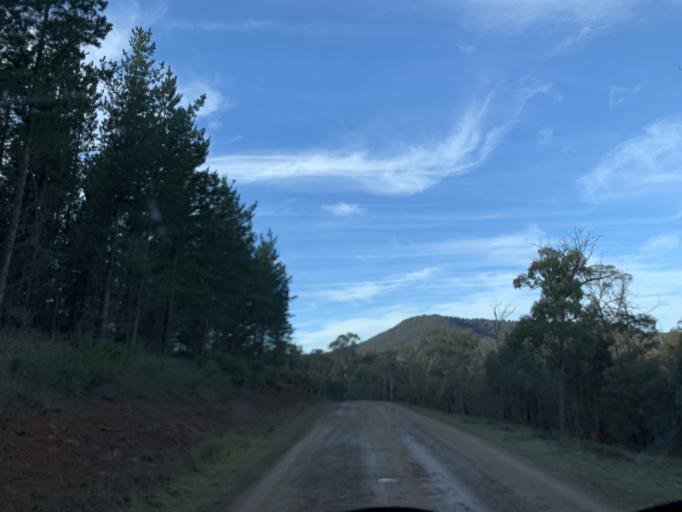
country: AU
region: Victoria
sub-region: Mansfield
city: Mansfield
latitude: -36.9194
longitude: 146.1039
